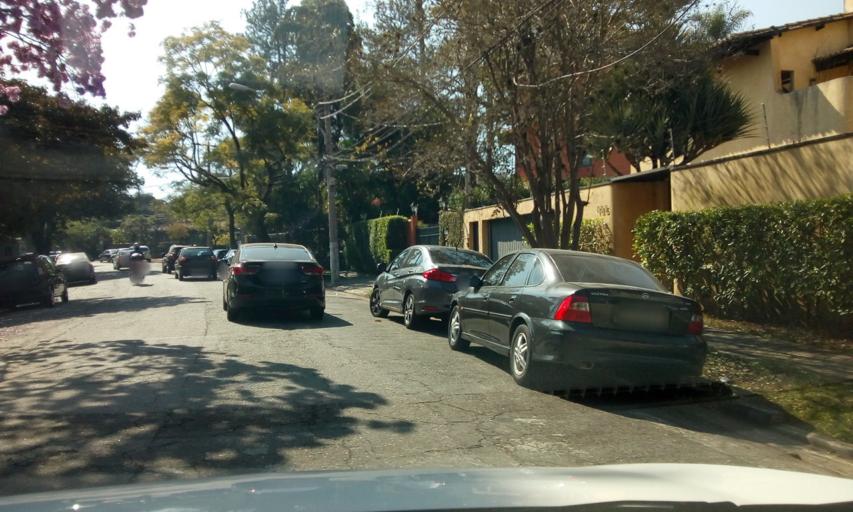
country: BR
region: Sao Paulo
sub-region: Sao Paulo
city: Sao Paulo
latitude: -23.5542
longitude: -46.7067
